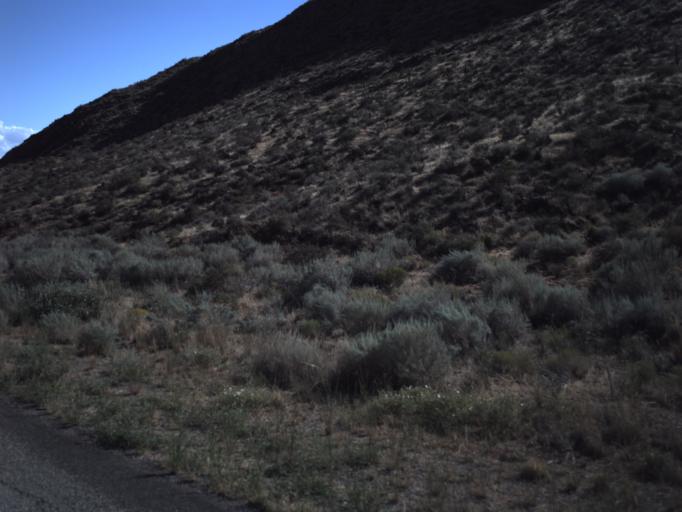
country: US
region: Utah
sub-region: Washington County
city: Toquerville
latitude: 37.2721
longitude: -113.2967
